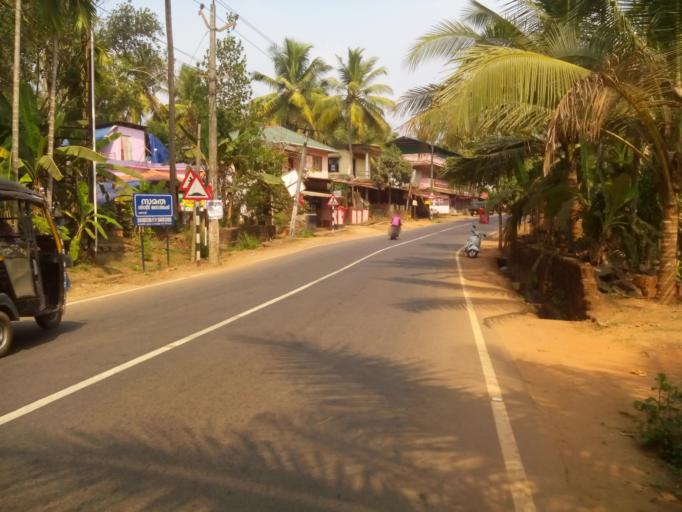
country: IN
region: Kerala
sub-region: Kozhikode
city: Naduvannur
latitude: 11.5845
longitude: 75.7647
